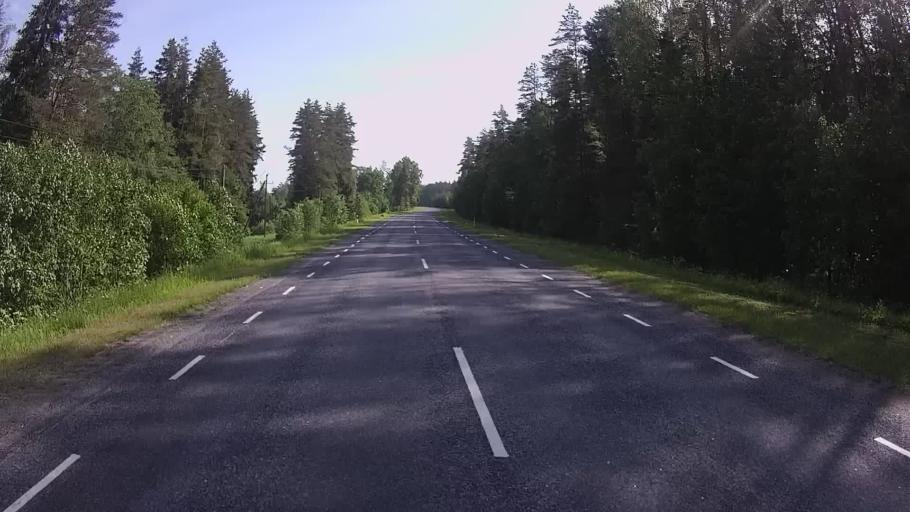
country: EE
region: Valgamaa
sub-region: Torva linn
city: Torva
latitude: 58.0245
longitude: 25.9573
